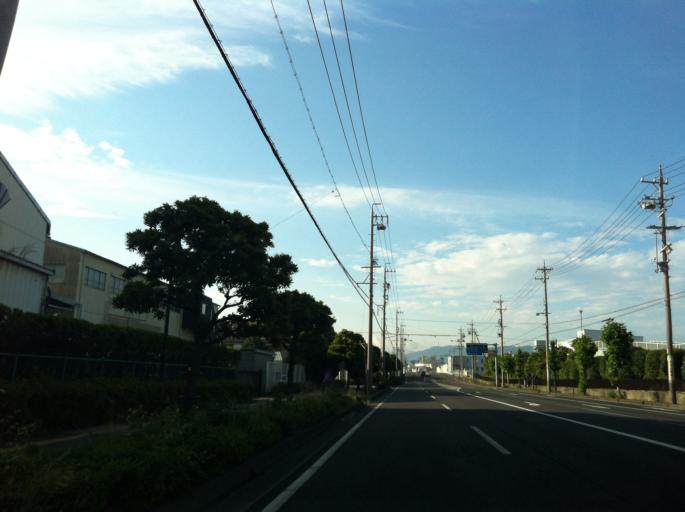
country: JP
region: Shizuoka
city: Shizuoka-shi
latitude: 34.9969
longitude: 138.4949
